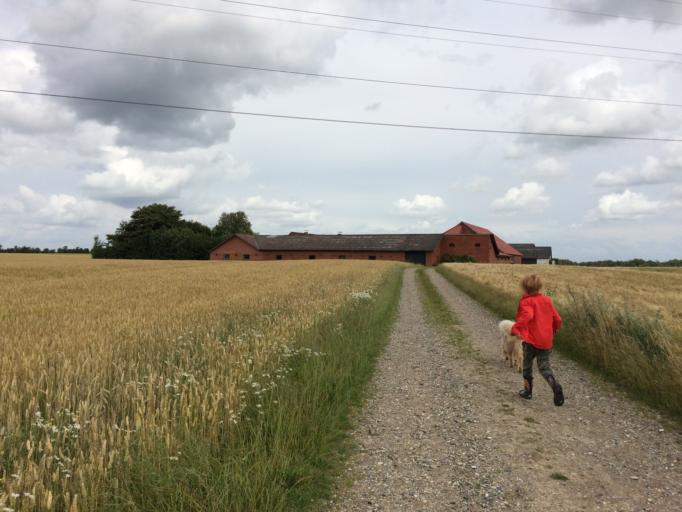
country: DK
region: Central Jutland
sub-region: Viborg Kommune
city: Viborg
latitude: 56.5002
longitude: 9.5238
